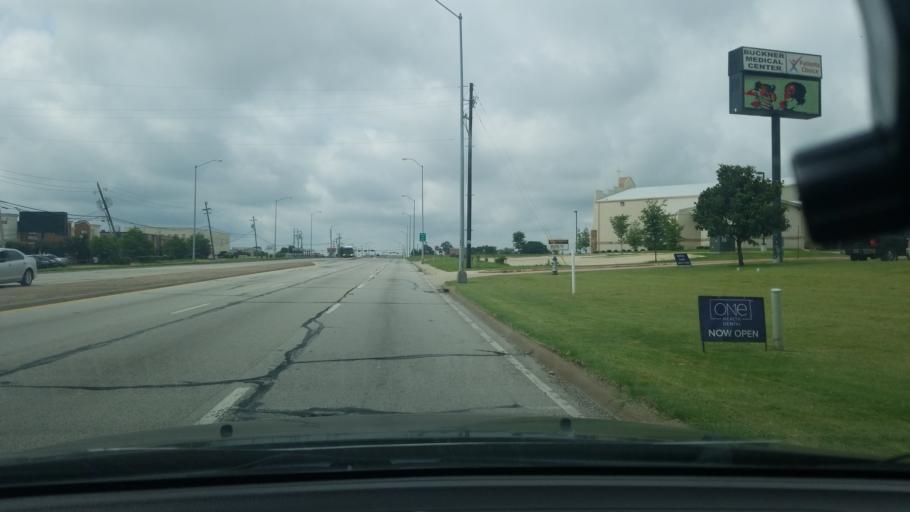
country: US
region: Texas
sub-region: Dallas County
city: Balch Springs
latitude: 32.7813
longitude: -96.6829
